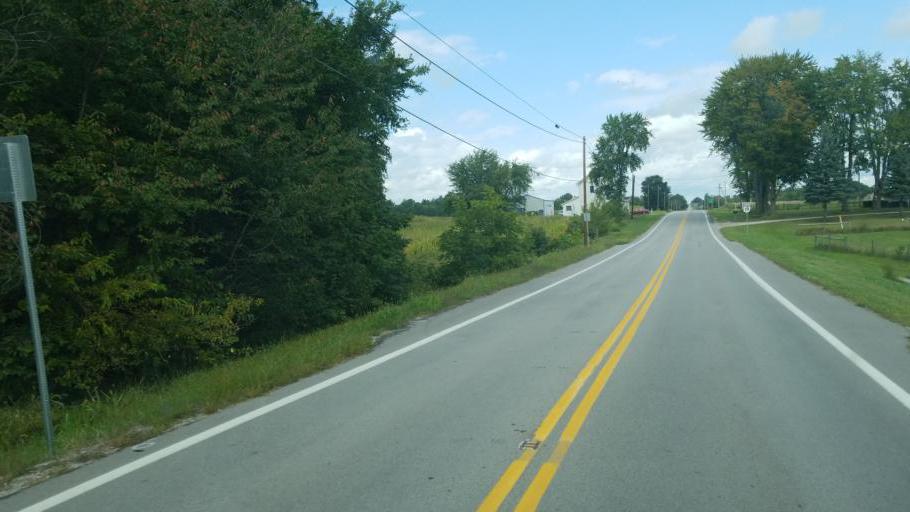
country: US
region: Ohio
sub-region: Seneca County
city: Tiffin
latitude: 41.0570
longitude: -83.0153
